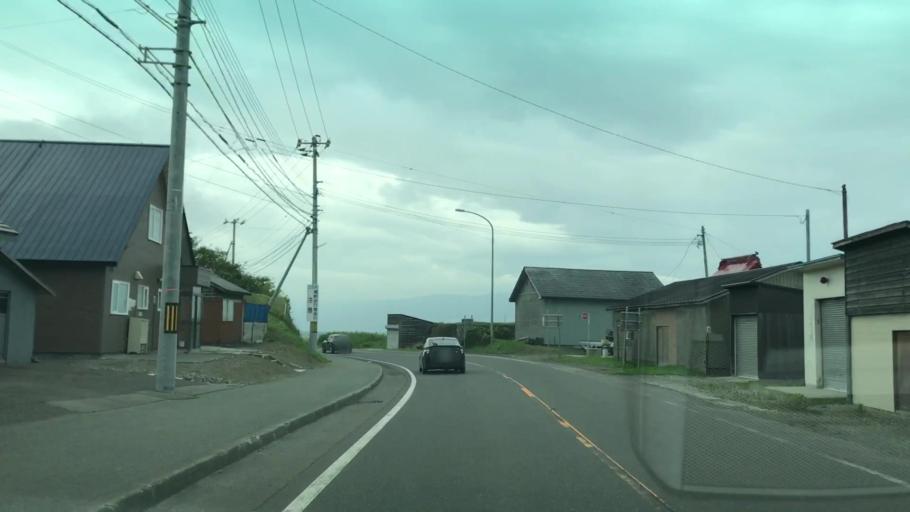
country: JP
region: Hokkaido
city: Iwanai
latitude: 42.8284
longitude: 140.3072
